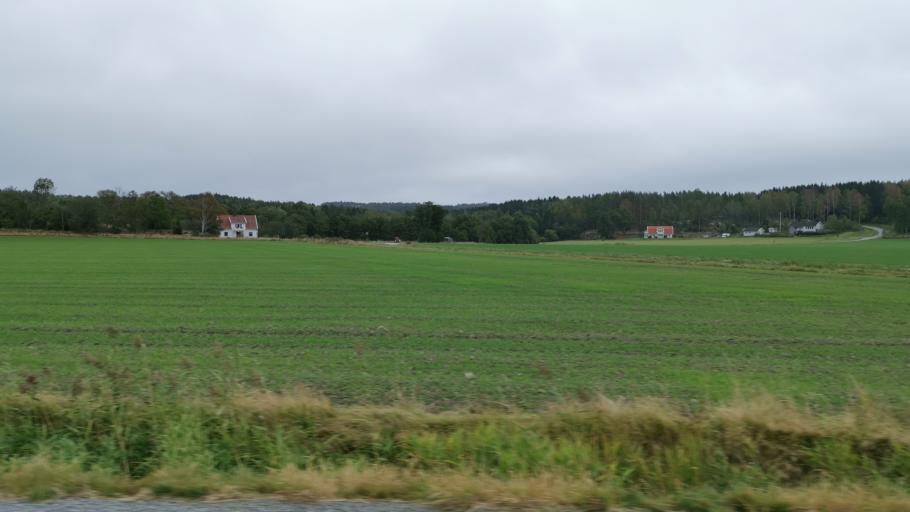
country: SE
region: Vaestra Goetaland
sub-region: Tanums Kommun
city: Tanumshede
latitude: 58.6214
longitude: 11.3562
